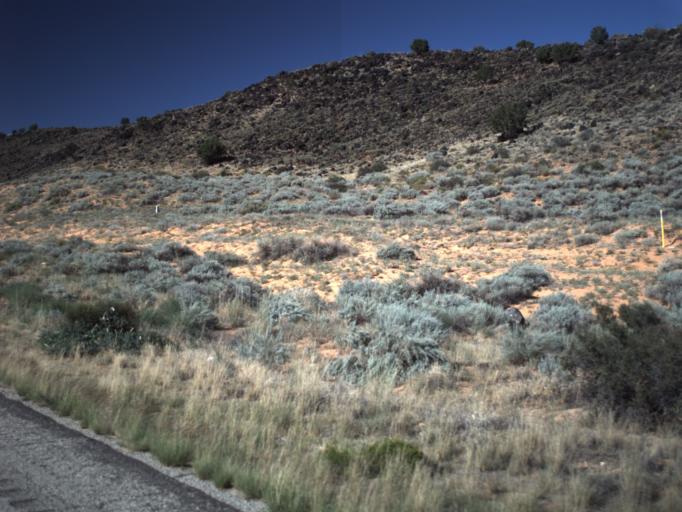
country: US
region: Utah
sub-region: Washington County
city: Toquerville
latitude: 37.2643
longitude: -113.2952
